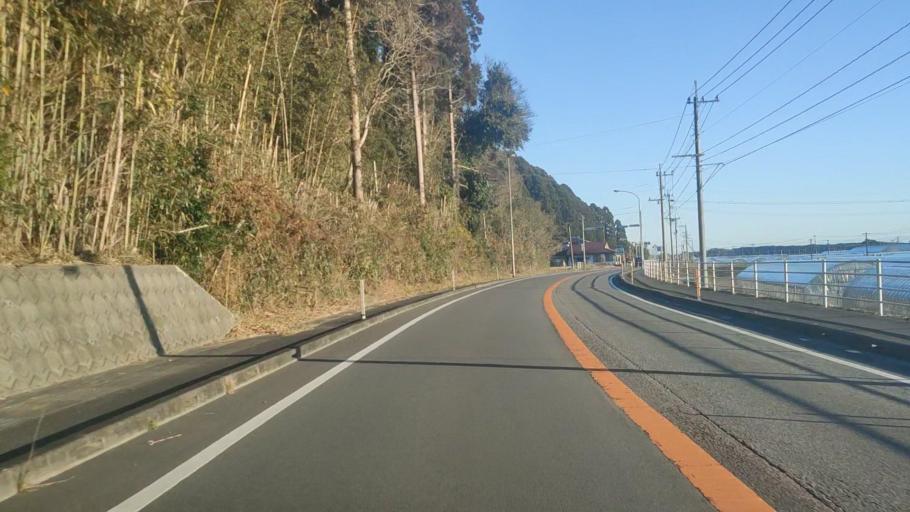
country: JP
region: Miyazaki
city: Takanabe
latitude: 32.0878
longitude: 131.5125
